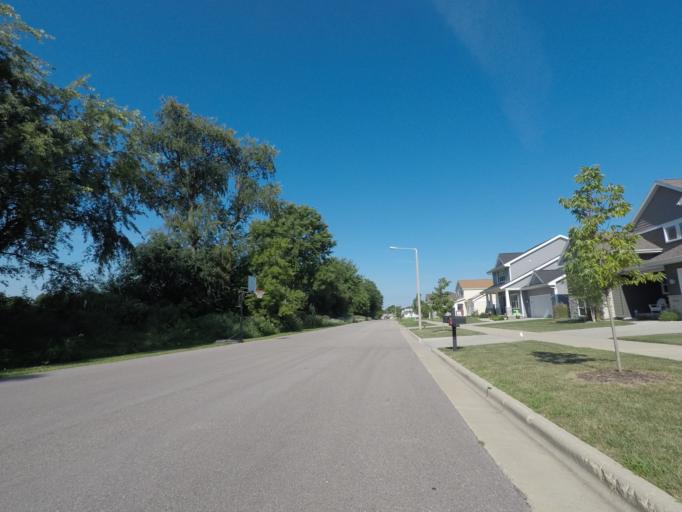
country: US
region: Wisconsin
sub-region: Dane County
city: Middleton
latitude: 43.0640
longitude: -89.5473
